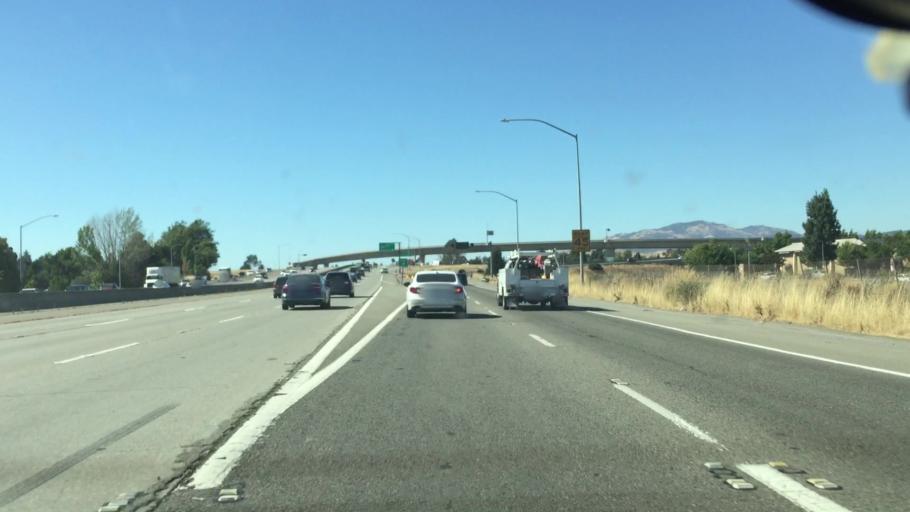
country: US
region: California
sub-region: Alameda County
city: Dublin
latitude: 37.6966
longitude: -121.9207
